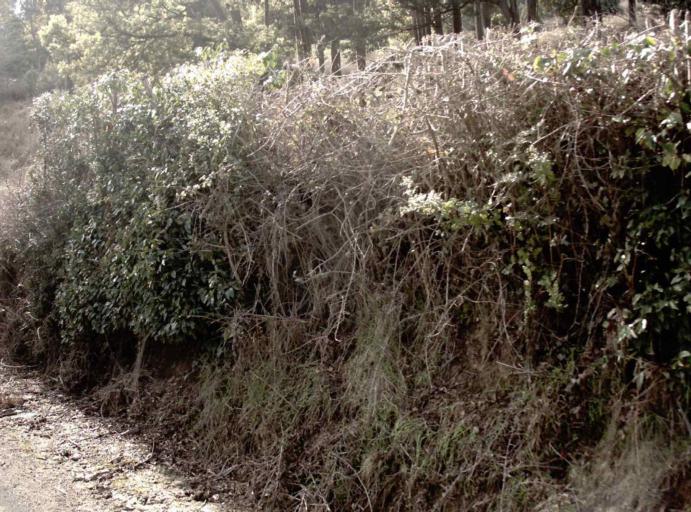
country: AU
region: Tasmania
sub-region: Launceston
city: Mayfield
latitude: -41.2453
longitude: 147.2464
